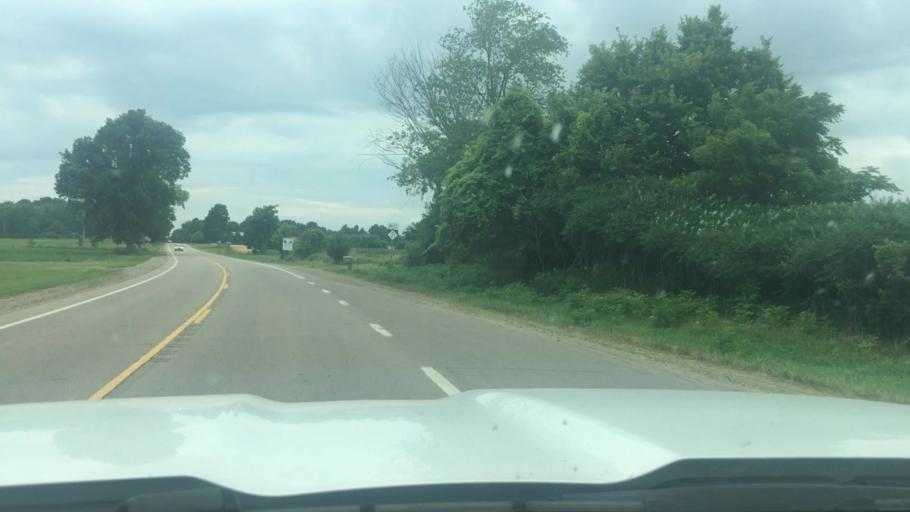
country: US
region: Michigan
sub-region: Clinton County
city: Fowler
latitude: 43.0018
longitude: -84.8743
